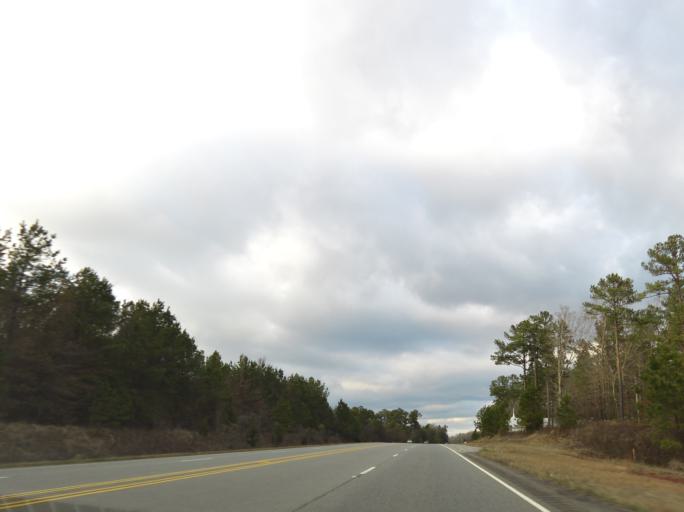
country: US
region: Georgia
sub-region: Houston County
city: Robins Air Force Base
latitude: 32.5349
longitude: -83.4405
